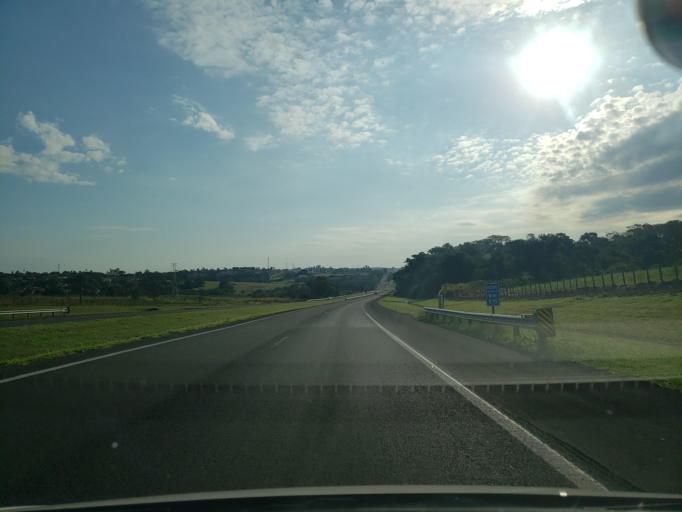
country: BR
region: Sao Paulo
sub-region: Valparaiso
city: Valparaiso
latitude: -21.2167
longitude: -50.8523
